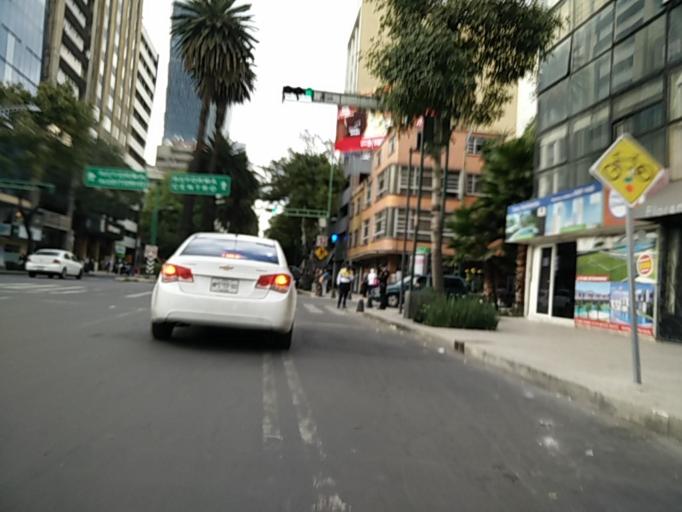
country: MX
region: Mexico City
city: Benito Juarez
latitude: 19.4233
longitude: -99.1656
